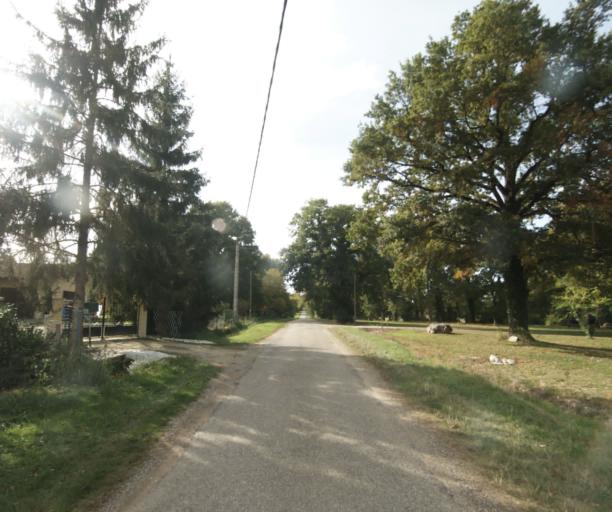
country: FR
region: Midi-Pyrenees
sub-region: Departement du Gers
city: Gondrin
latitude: 43.8696
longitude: 0.2082
